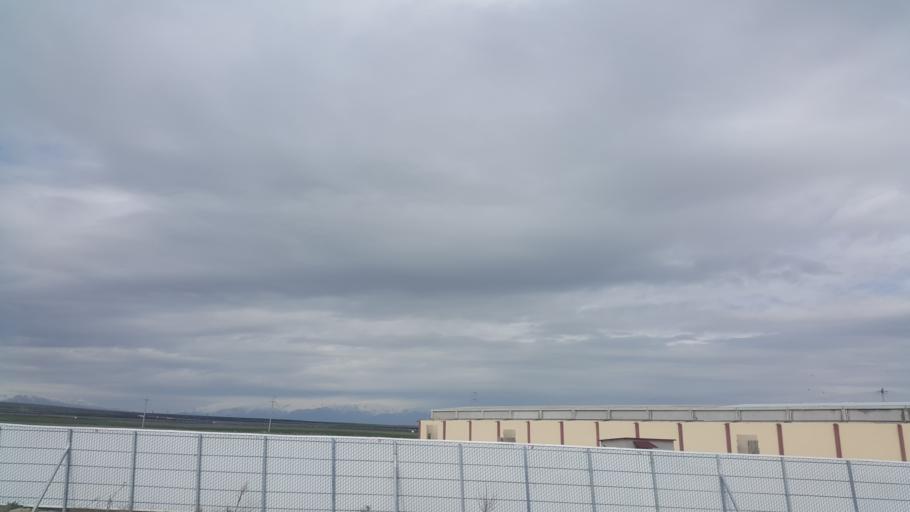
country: TR
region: Nigde
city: Altunhisar
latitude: 37.8253
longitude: 34.1975
